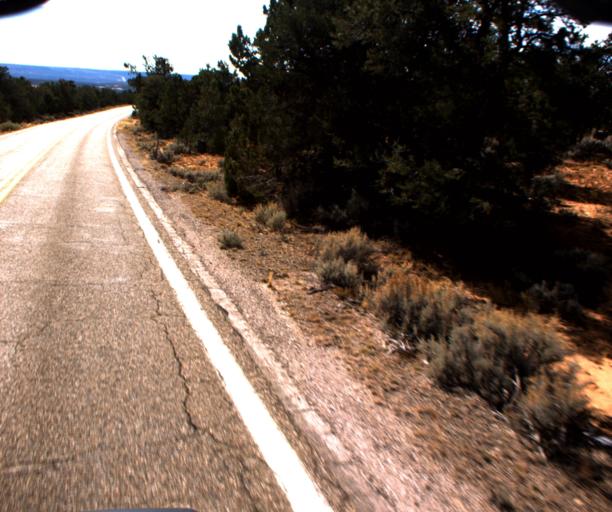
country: US
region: Arizona
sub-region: Navajo County
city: Kayenta
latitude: 36.6315
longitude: -110.5092
